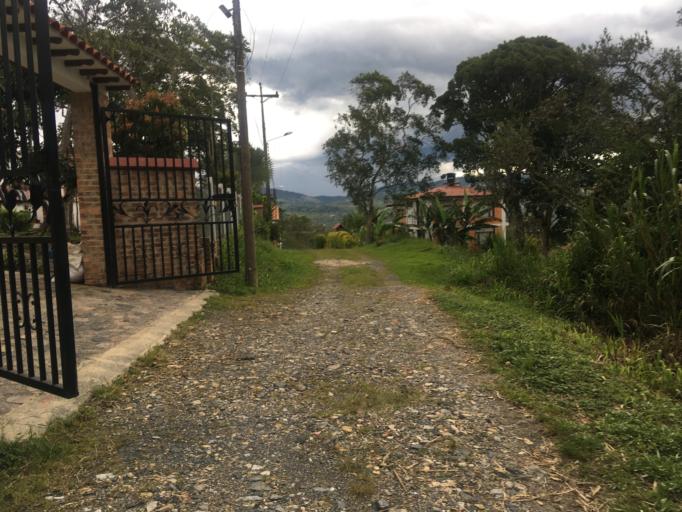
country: CO
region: Santander
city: Barbosa
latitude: 5.9175
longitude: -73.6044
